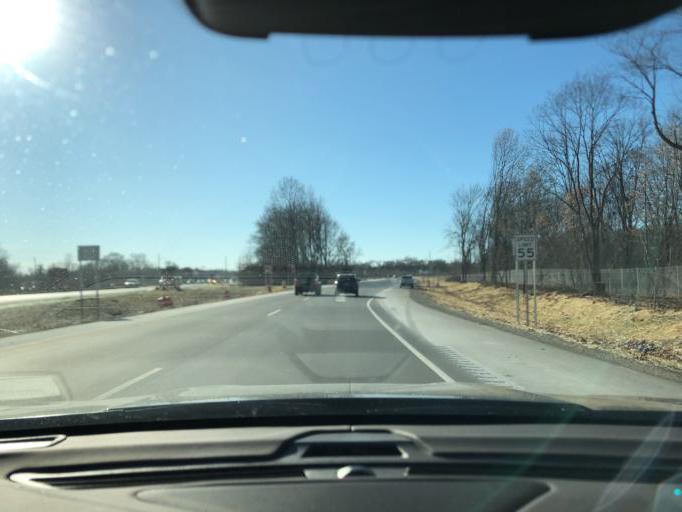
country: US
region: Michigan
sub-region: Washtenaw County
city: Ypsilanti
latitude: 42.2415
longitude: -83.5674
